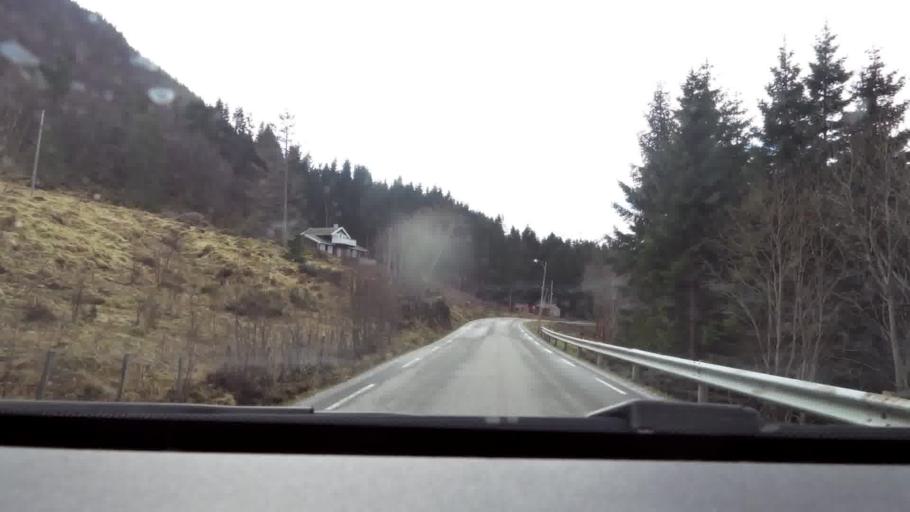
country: NO
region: More og Romsdal
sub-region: Eide
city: Eide
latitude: 62.9176
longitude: 7.5497
